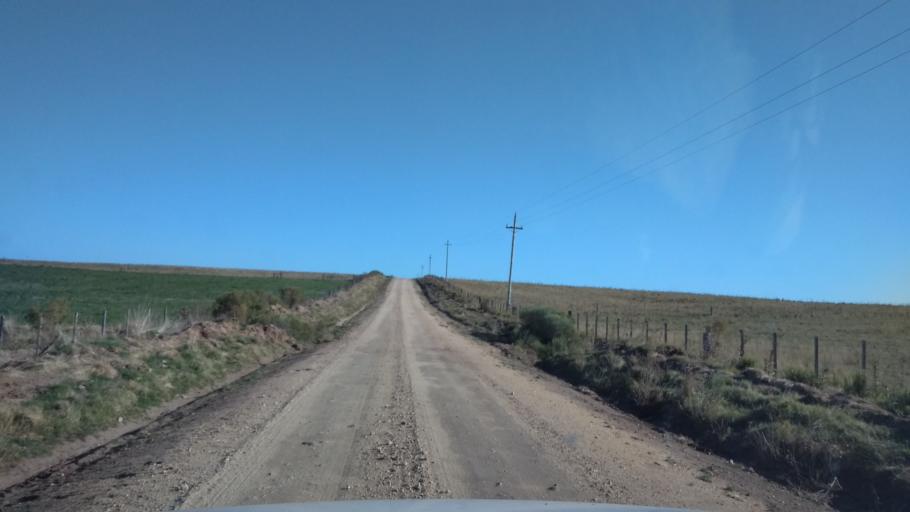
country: UY
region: Florida
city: Casupa
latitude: -34.0083
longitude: -55.7871
